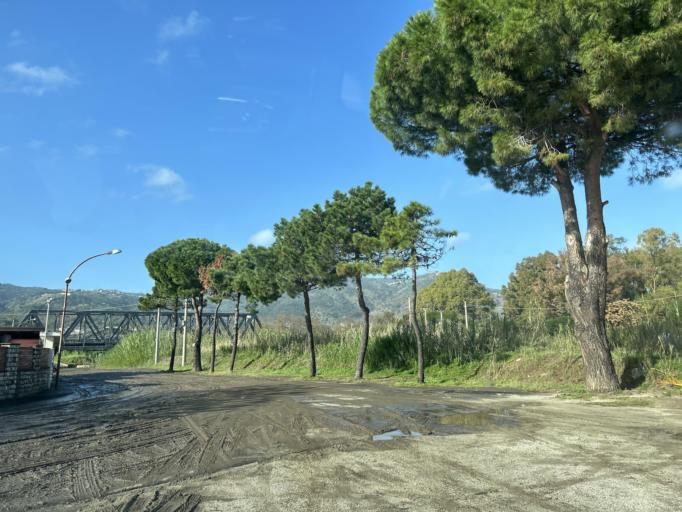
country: IT
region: Calabria
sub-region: Provincia di Catanzaro
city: Montepaone Lido
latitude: 38.7119
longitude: 16.5339
